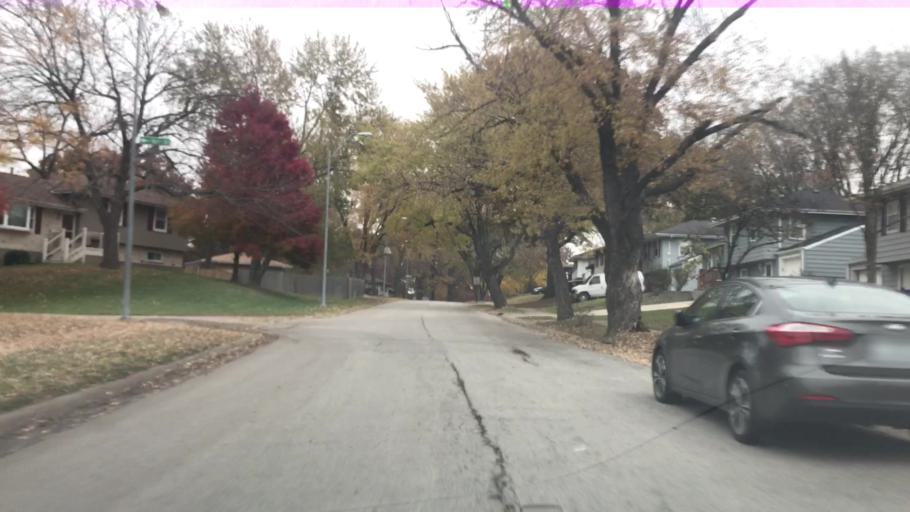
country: US
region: Missouri
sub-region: Clay County
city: Claycomo
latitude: 39.1954
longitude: -94.4887
